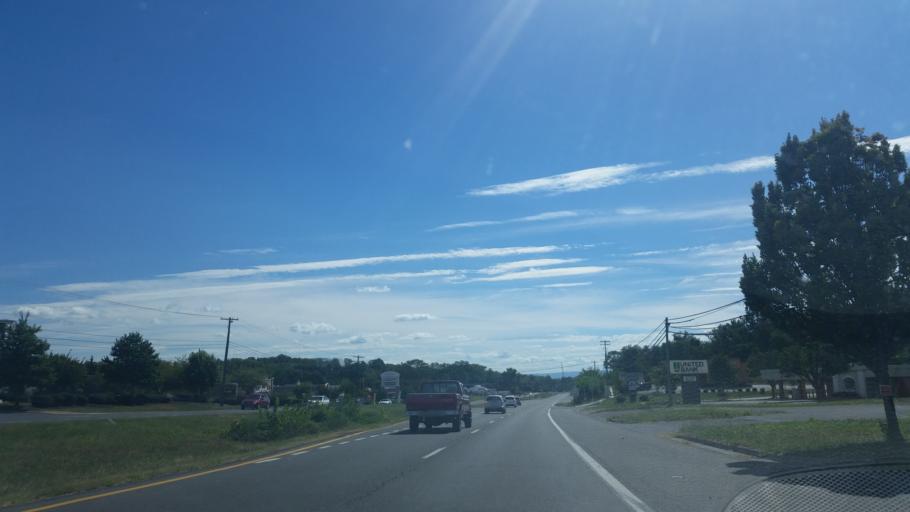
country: US
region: Virginia
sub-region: City of Winchester
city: Winchester
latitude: 39.2097
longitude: -78.1783
